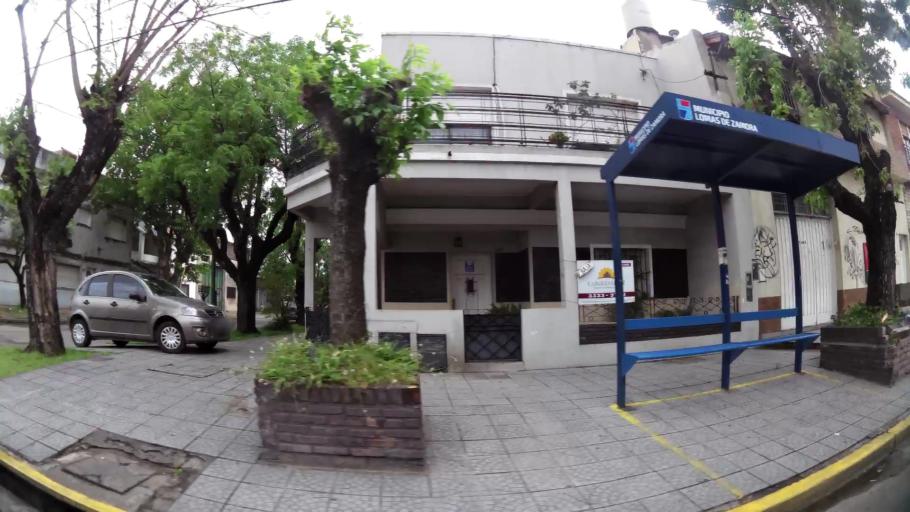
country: AR
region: Buenos Aires
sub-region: Partido de Lomas de Zamora
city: Lomas de Zamora
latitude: -34.7595
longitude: -58.3829
